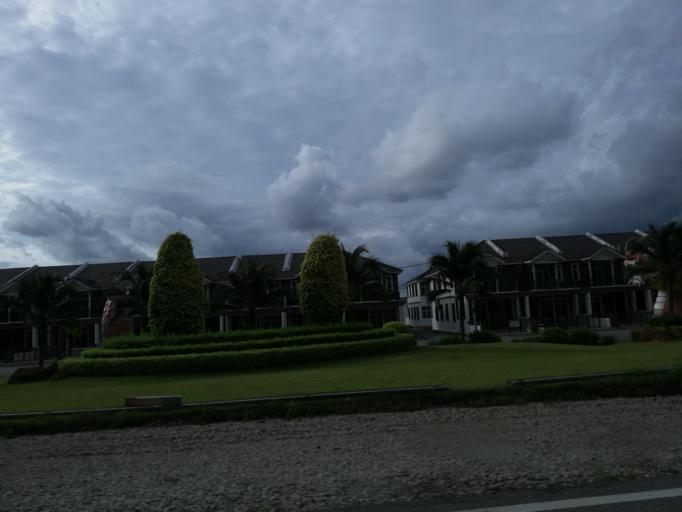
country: MY
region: Penang
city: Tasek Glugor
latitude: 5.5055
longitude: 100.6211
